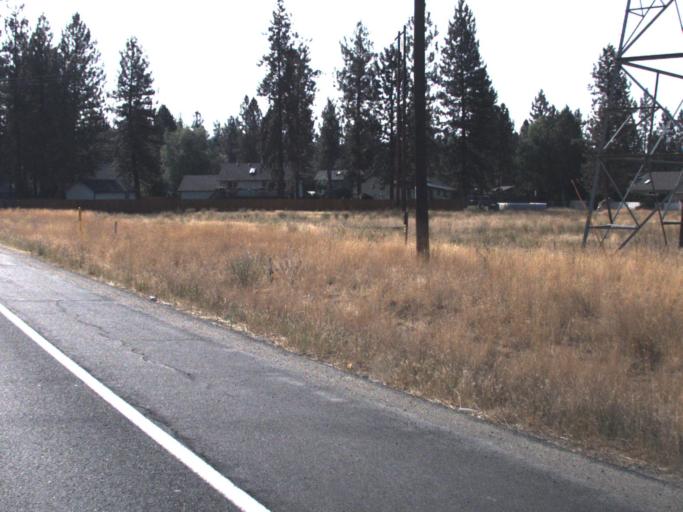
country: US
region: Washington
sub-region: Spokane County
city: Town and Country
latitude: 47.7542
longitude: -117.5150
